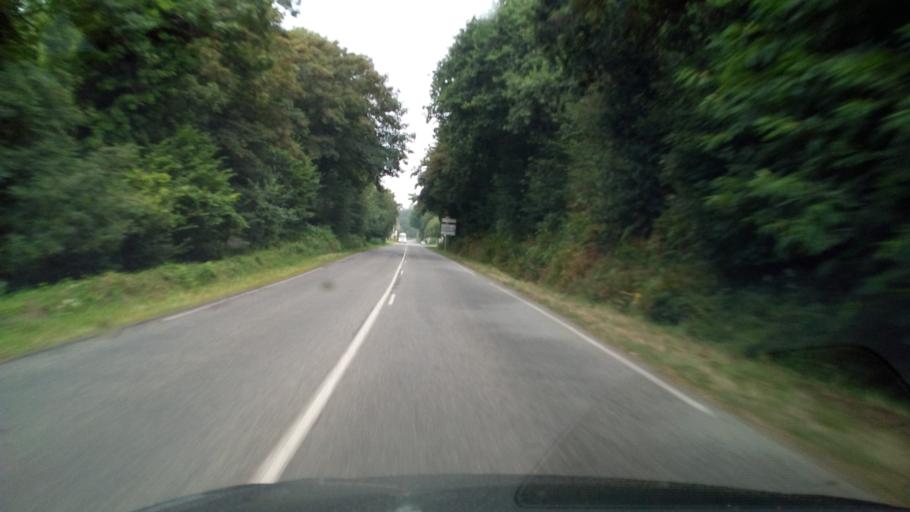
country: FR
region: Brittany
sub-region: Departement du Finistere
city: Landivisiau
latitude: 48.4989
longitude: -4.0911
